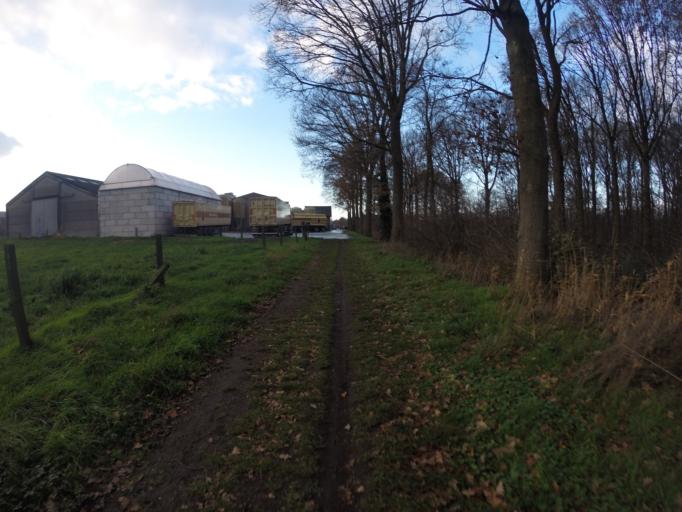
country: BE
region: Flanders
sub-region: Provincie West-Vlaanderen
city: Wingene
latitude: 51.0836
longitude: 3.3066
